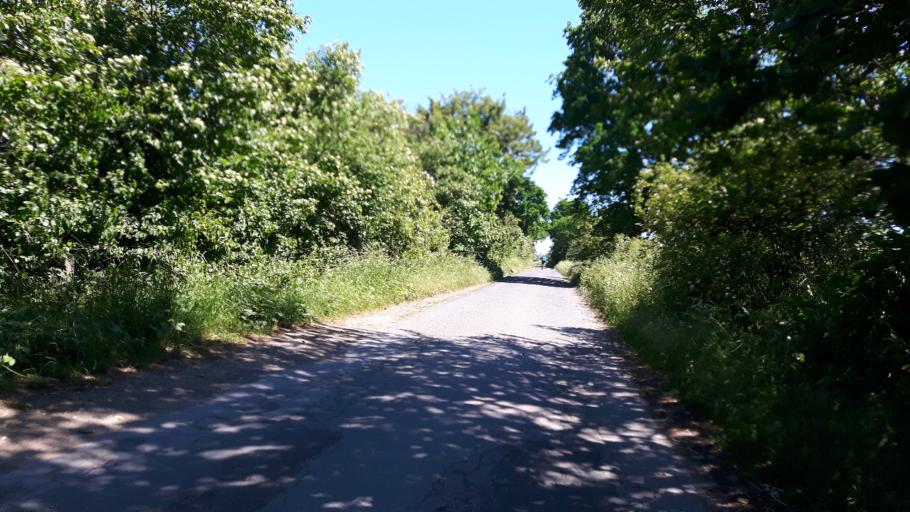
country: DE
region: North Rhine-Westphalia
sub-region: Regierungsbezirk Dusseldorf
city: Ratingen
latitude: 51.3126
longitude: 6.7810
